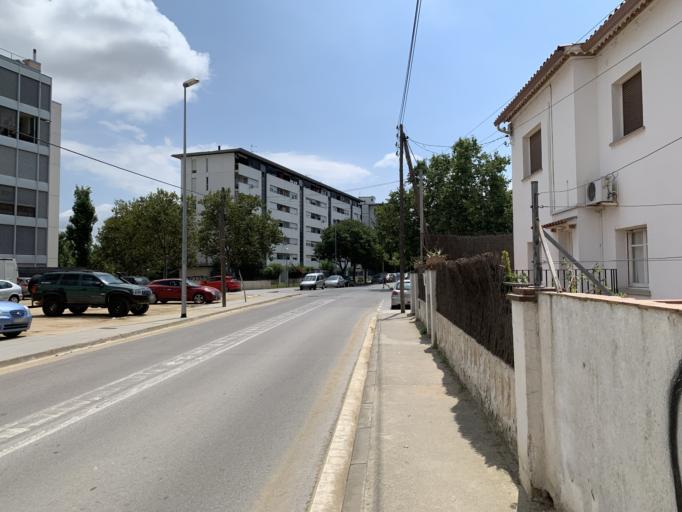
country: ES
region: Catalonia
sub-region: Provincia de Barcelona
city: Cerdanyola del Valles
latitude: 41.4980
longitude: 2.1286
